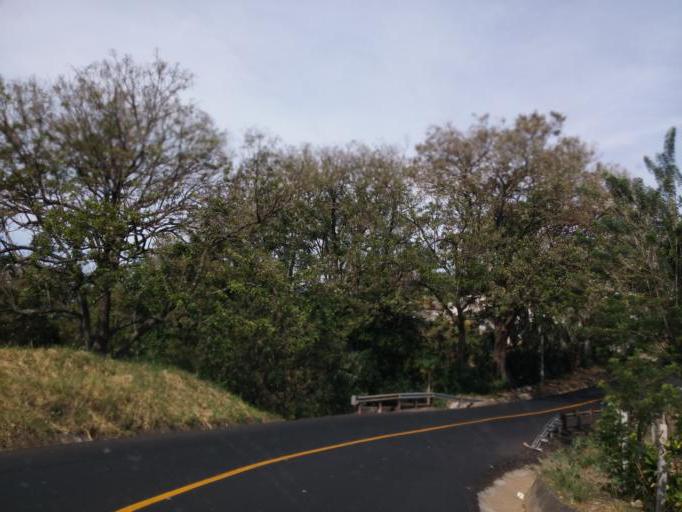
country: CR
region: Alajuela
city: Alajuela
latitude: 10.0260
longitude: -84.2217
